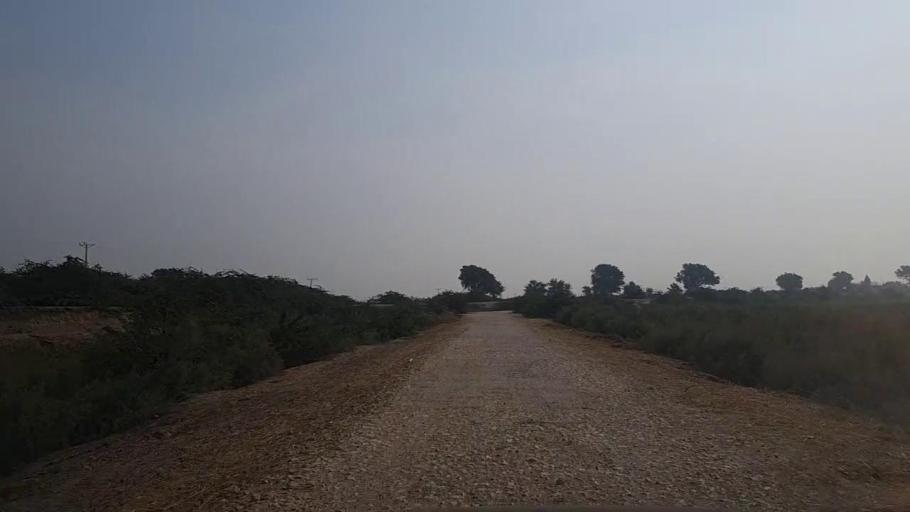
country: PK
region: Sindh
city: Mirpur Sakro
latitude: 24.3767
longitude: 67.7557
